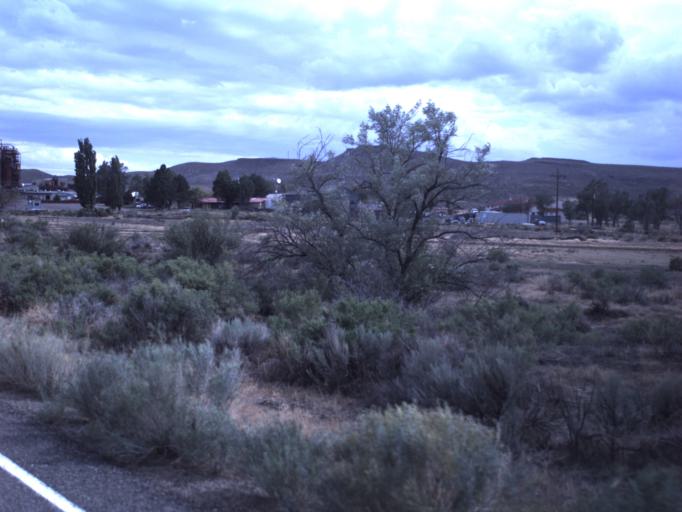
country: US
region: Colorado
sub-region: Rio Blanco County
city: Rangely
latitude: 40.0224
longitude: -109.1746
